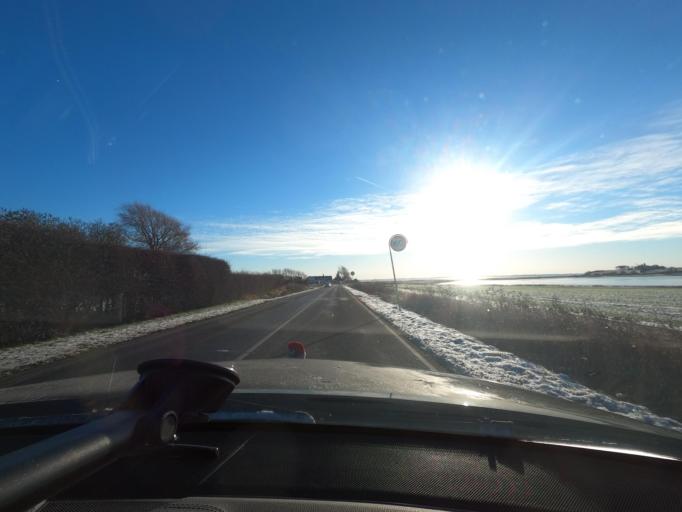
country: DE
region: Schleswig-Holstein
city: Pommerby
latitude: 54.8628
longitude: 9.9981
